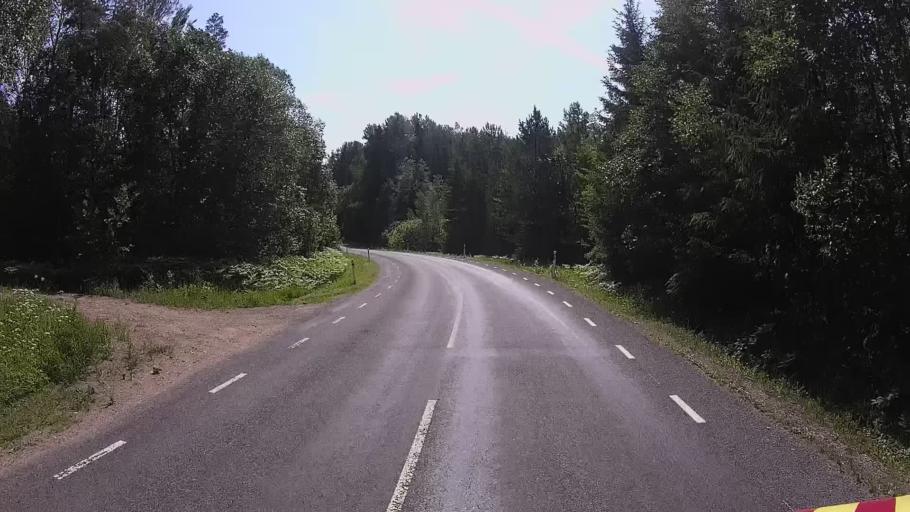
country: EE
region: Viljandimaa
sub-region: Karksi vald
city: Karksi-Nuia
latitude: 58.0376
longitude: 25.5464
